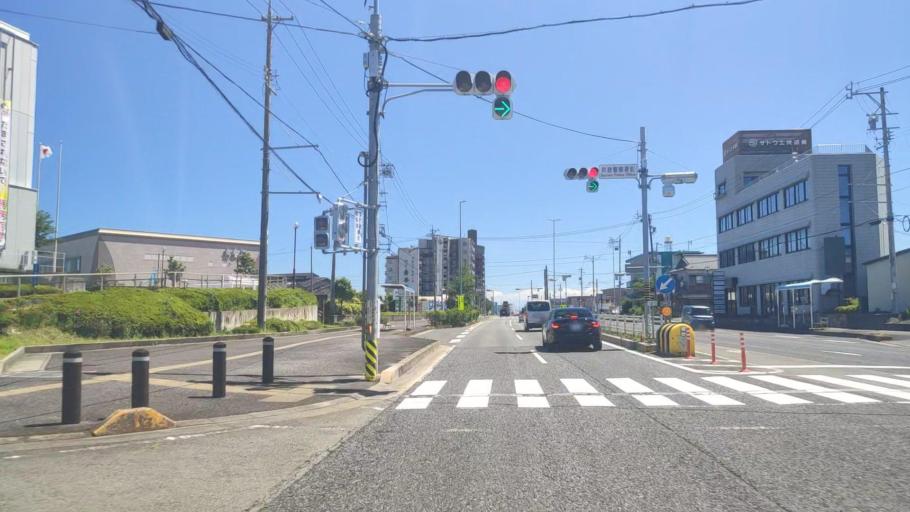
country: JP
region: Mie
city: Suzuka
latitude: 34.8477
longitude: 136.5894
